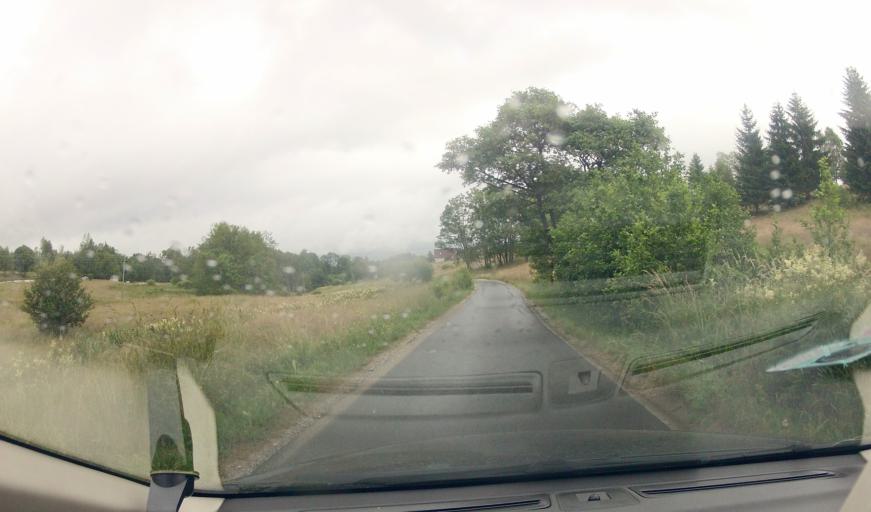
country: PL
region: Lower Silesian Voivodeship
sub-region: Powiat klodzki
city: Miedzylesie
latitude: 50.1179
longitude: 16.6325
